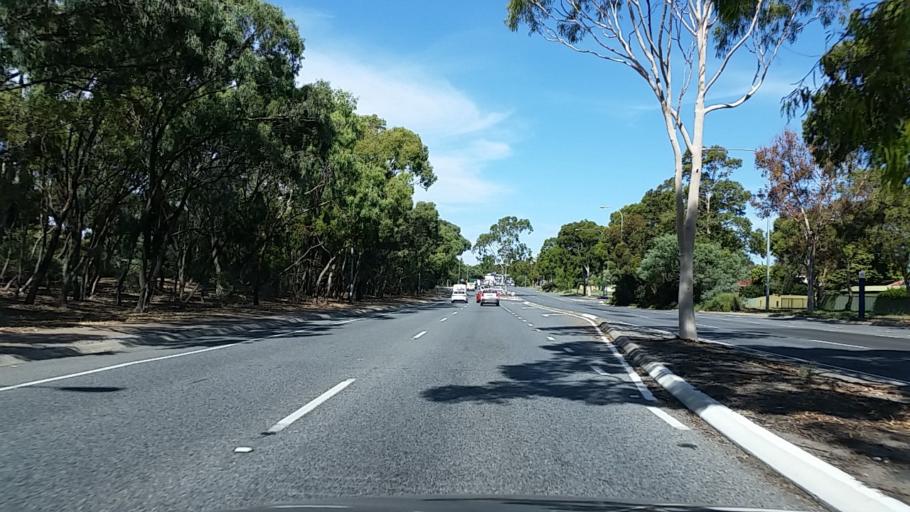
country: AU
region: South Australia
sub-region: Salisbury
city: Ingle Farm
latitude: -34.8243
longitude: 138.6301
